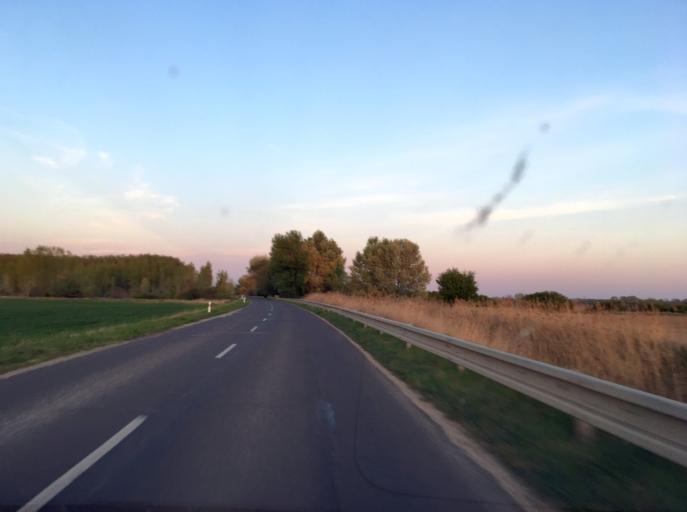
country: SK
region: Nitriansky
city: Kolarovo
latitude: 47.9177
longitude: 18.0468
